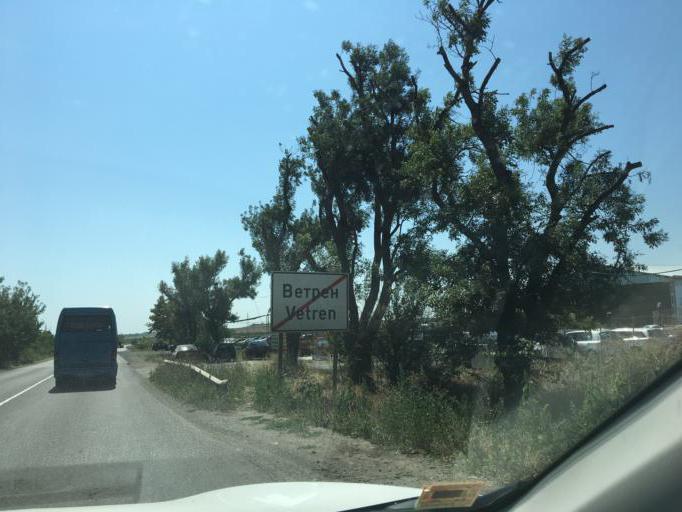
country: BG
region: Burgas
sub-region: Obshtina Kameno
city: Kameno
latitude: 42.5989
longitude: 27.3894
